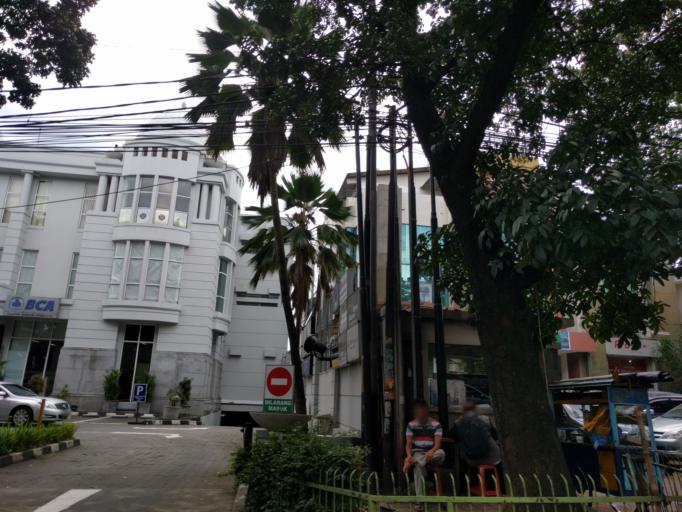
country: ID
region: West Java
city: Bogor
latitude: -6.6058
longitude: 106.8082
